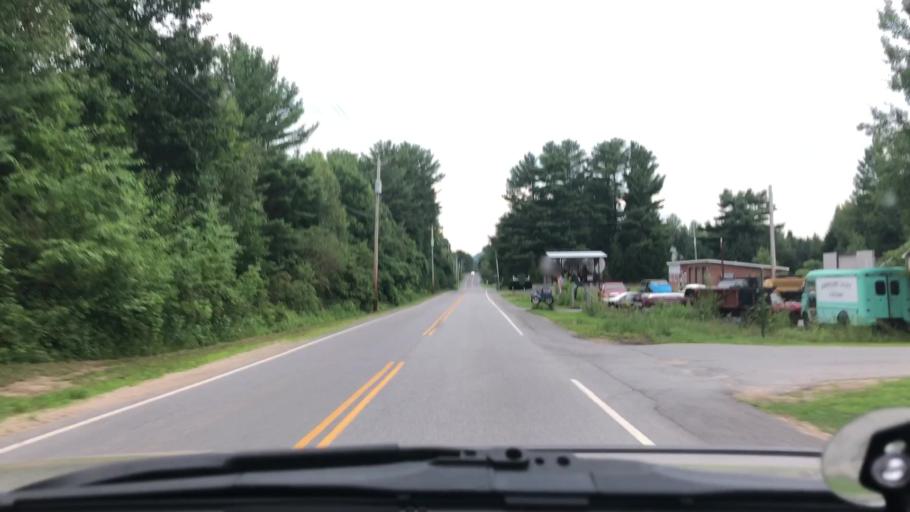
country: US
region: New York
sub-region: Saratoga County
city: Corinth
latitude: 43.2281
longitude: -73.8227
